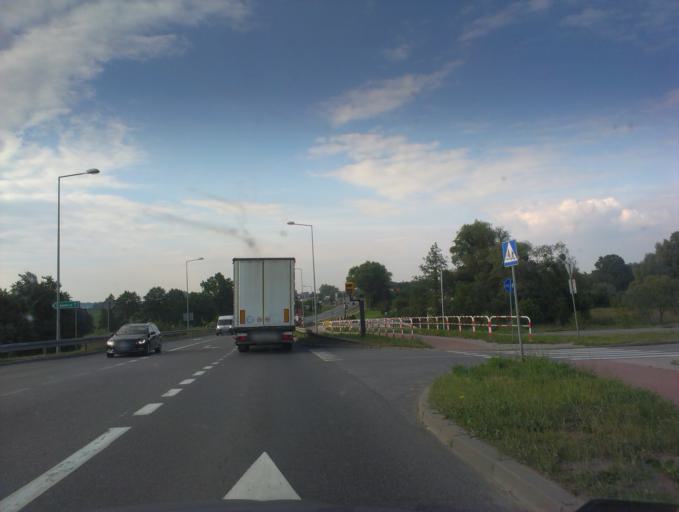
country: PL
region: Lower Silesian Voivodeship
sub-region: Powiat trzebnicki
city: Psary
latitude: 51.2467
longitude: 17.0441
